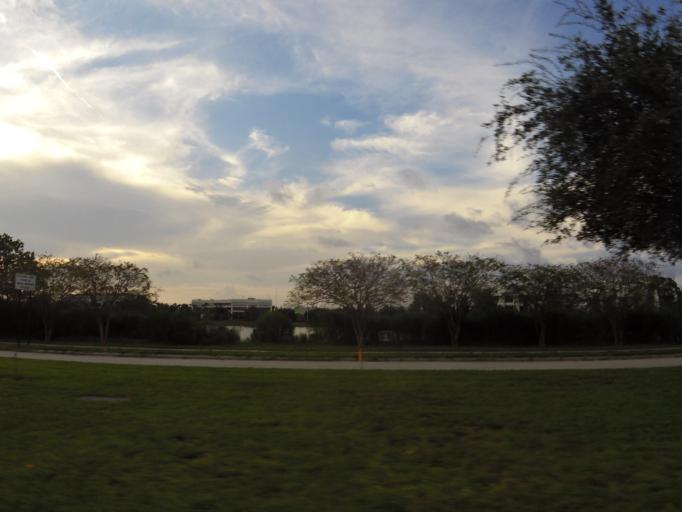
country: US
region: Florida
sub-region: Saint Johns County
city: Ponte Vedra Beach
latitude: 30.2443
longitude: -81.5310
